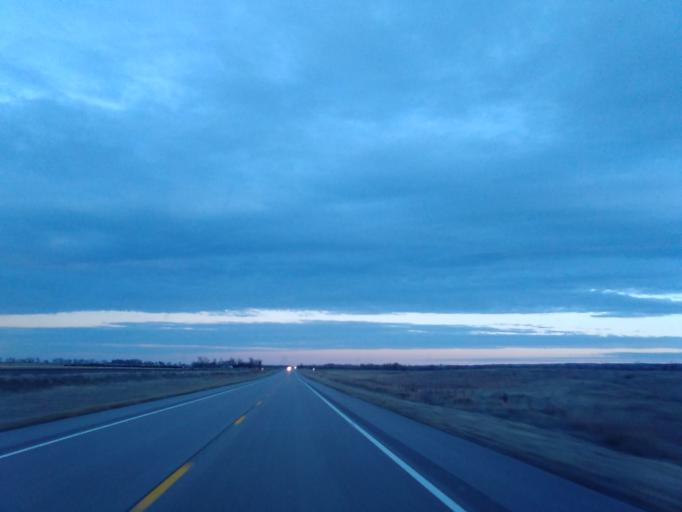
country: US
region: Nebraska
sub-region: Garden County
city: Oshkosh
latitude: 41.3706
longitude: -102.2438
